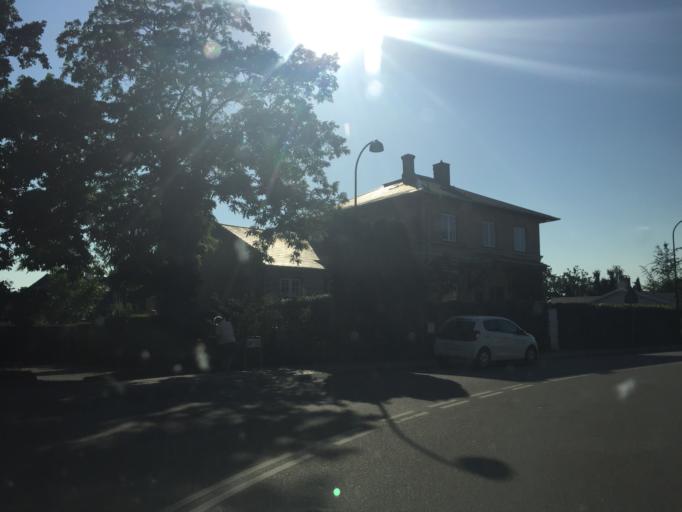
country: DK
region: Capital Region
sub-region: Gentofte Kommune
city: Charlottenlund
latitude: 55.7525
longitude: 12.5675
